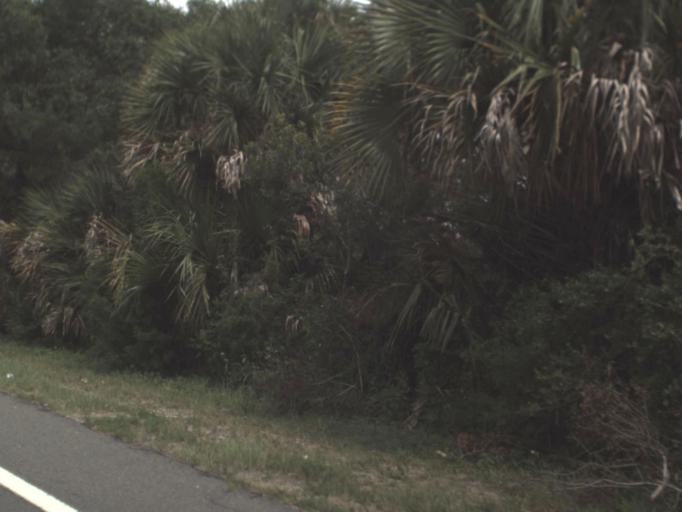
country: US
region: Florida
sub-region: Duval County
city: Atlantic Beach
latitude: 30.3980
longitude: -81.4675
